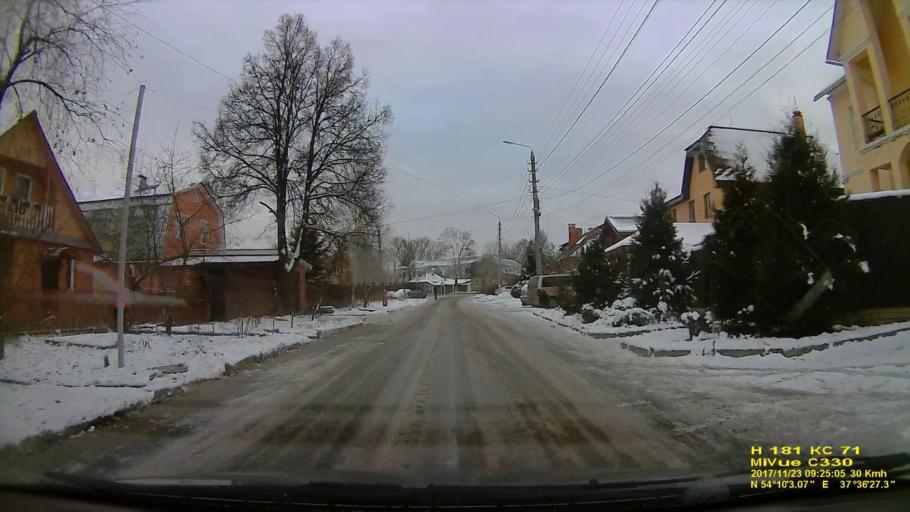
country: RU
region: Tula
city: Tula
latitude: 54.1674
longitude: 37.6075
